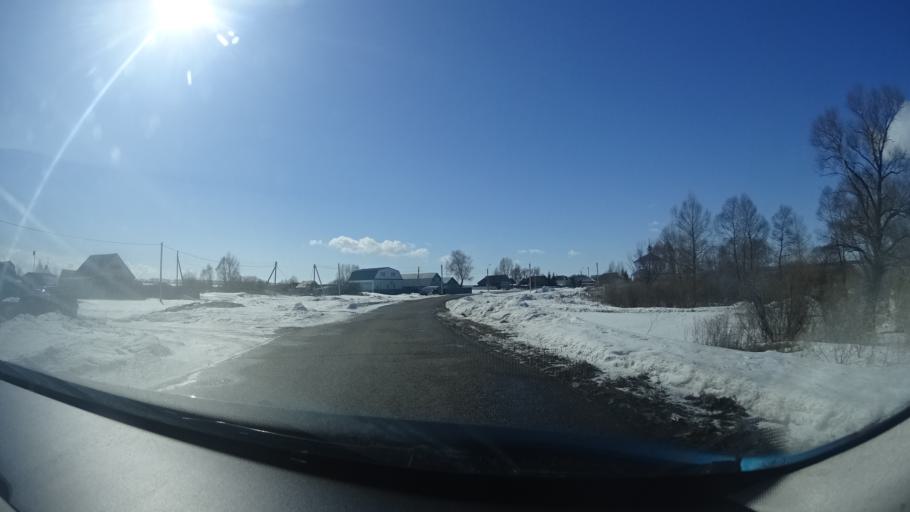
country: RU
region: Bashkortostan
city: Avdon
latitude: 54.5814
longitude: 55.8562
